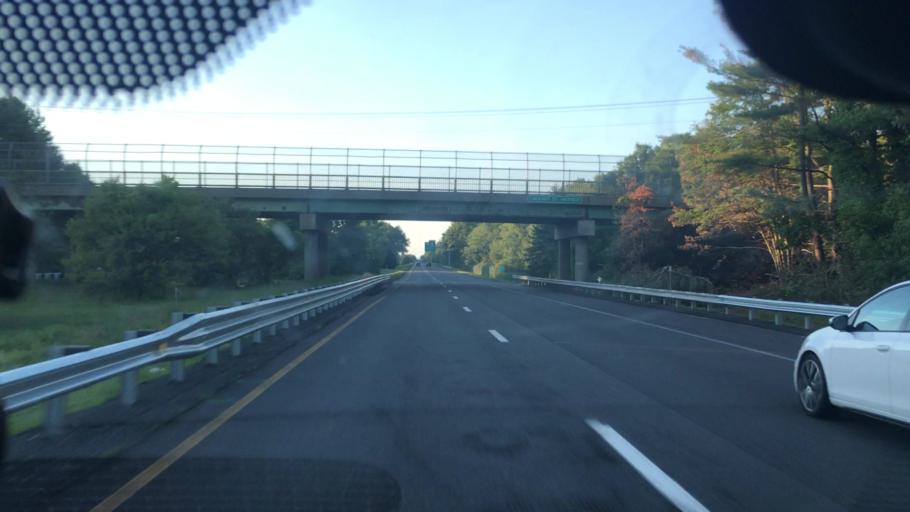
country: US
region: Massachusetts
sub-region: Hampshire County
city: Hatfield
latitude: 42.3812
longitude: -72.6314
